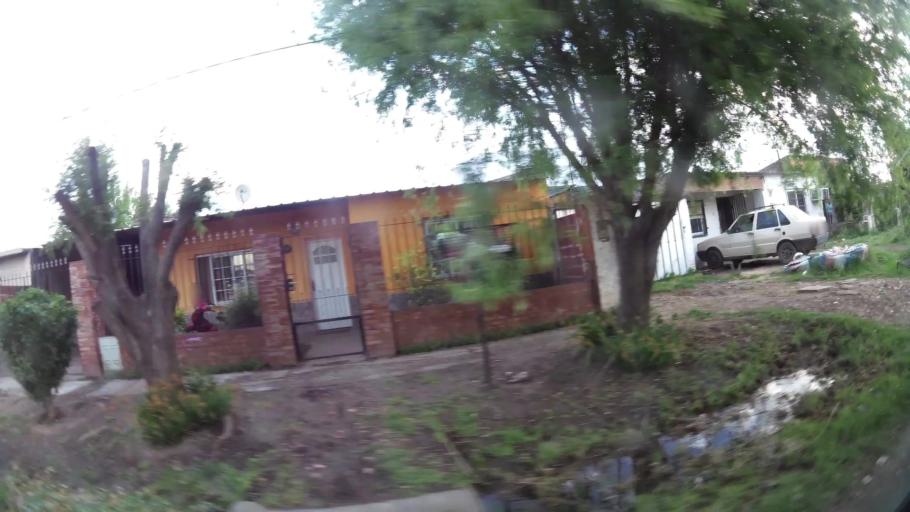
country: AR
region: Buenos Aires
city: San Nicolas de los Arroyos
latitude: -33.3163
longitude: -60.2473
